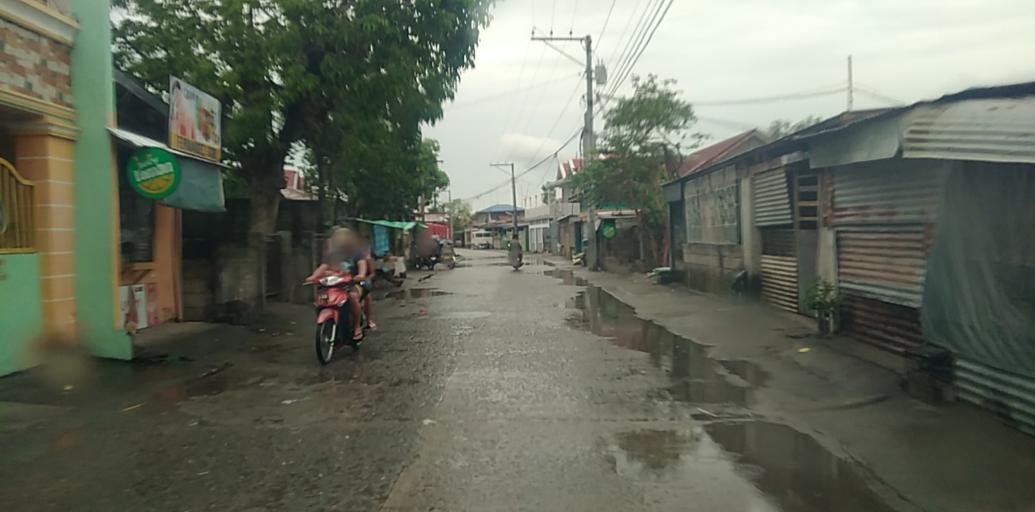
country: PH
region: Central Luzon
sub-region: Province of Pampanga
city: Arayat
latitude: 15.1374
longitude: 120.7393
